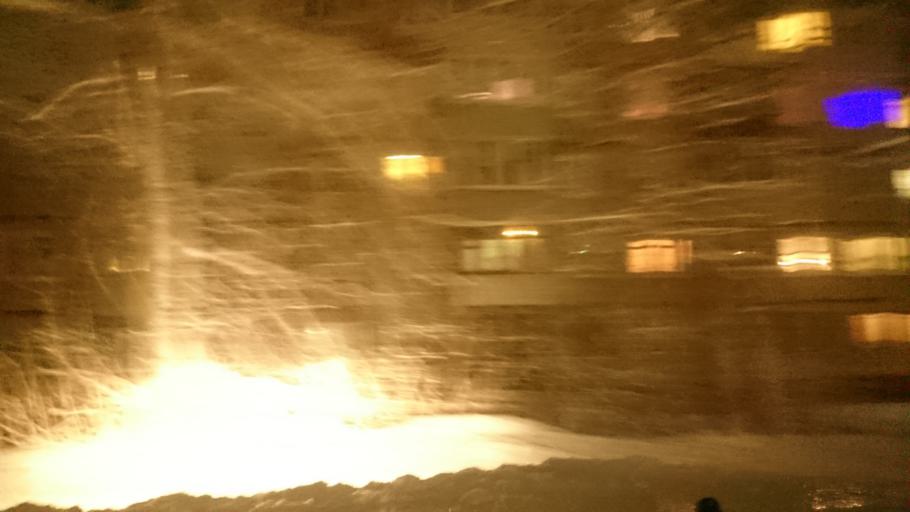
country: RU
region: Tula
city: Mendeleyevskiy
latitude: 54.1534
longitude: 37.5900
